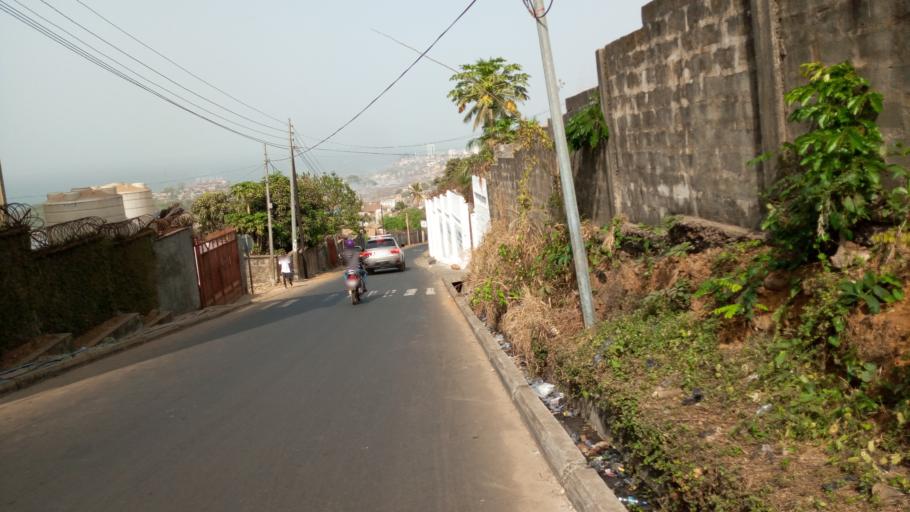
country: SL
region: Western Area
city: Freetown
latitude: 8.4795
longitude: -13.2613
